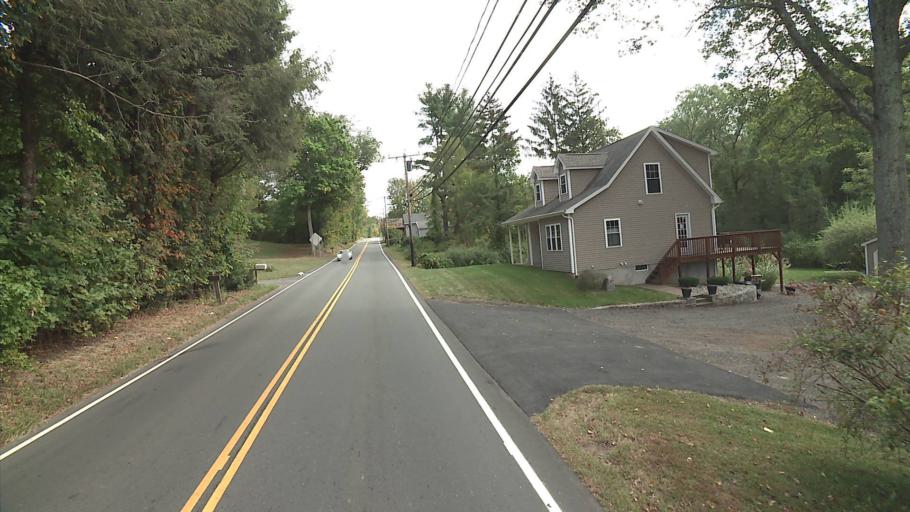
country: US
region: Connecticut
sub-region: Middlesex County
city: Durham
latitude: 41.4864
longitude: -72.6855
